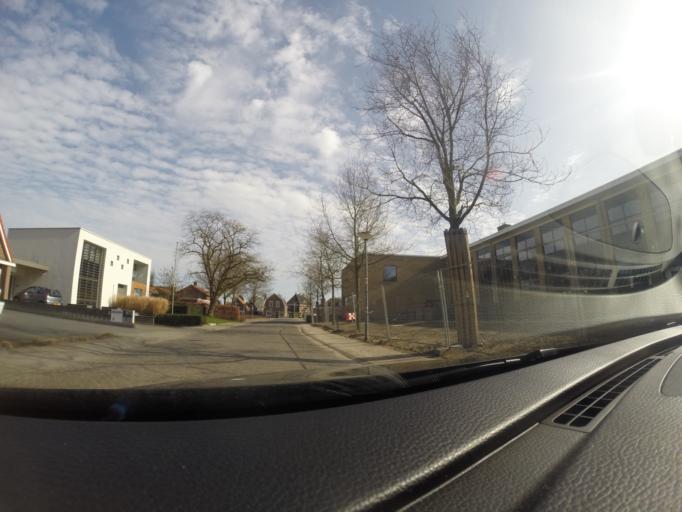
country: NL
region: Gelderland
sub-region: Berkelland
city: Eibergen
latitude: 52.0384
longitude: 6.6172
